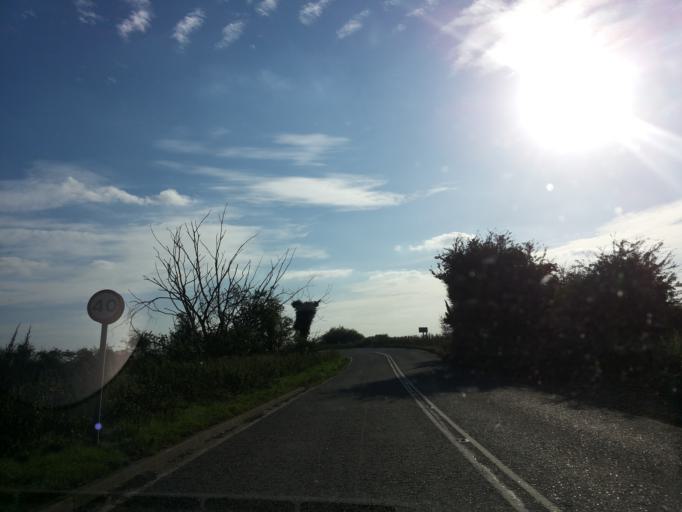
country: GB
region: England
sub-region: East Riding of Yorkshire
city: Rawcliffe
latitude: 53.6728
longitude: -0.9903
